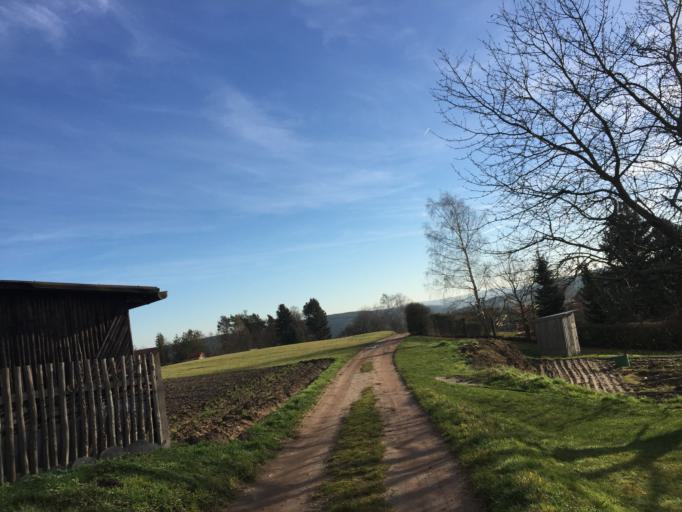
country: DE
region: Thuringia
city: Orlamunde
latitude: 50.7735
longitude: 11.5115
